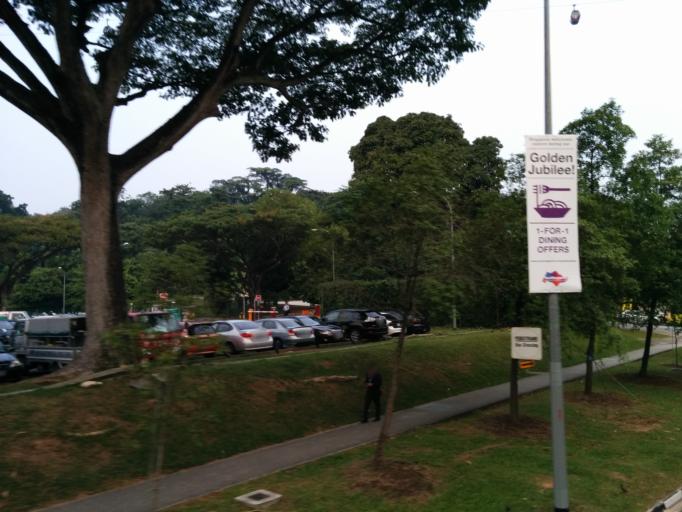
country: SG
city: Singapore
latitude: 1.2673
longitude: 103.8179
